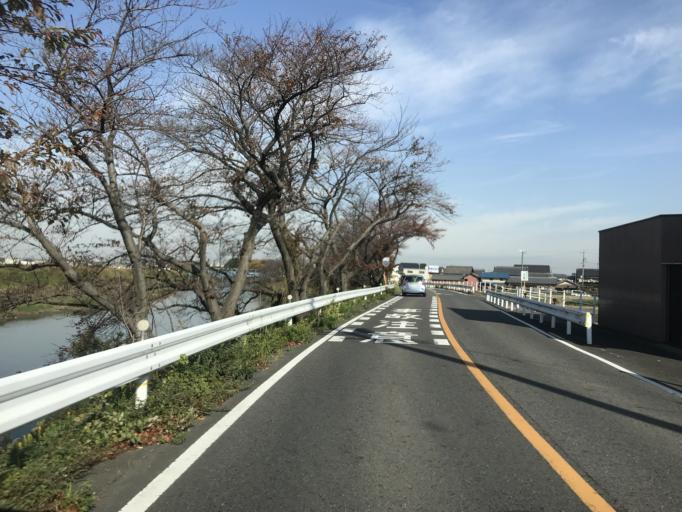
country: JP
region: Aichi
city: Iwakura
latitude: 35.2270
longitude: 136.8462
